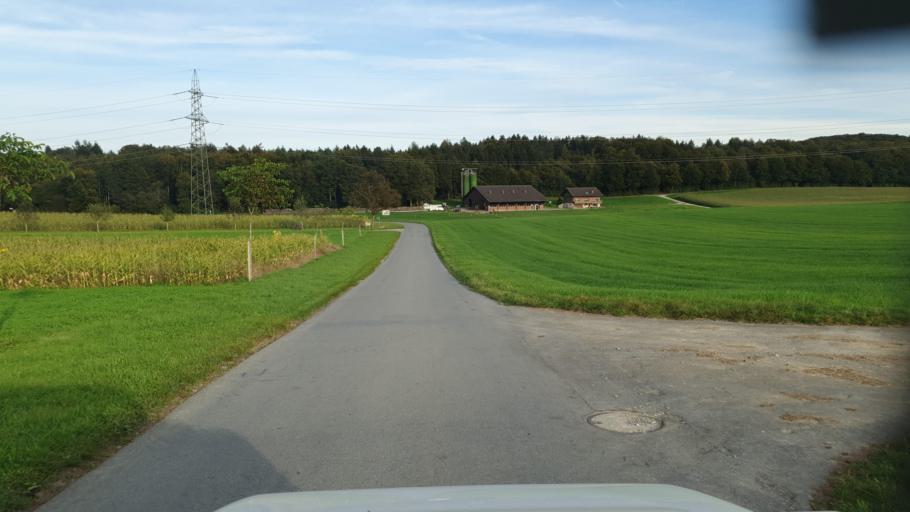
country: CH
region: Aargau
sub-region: Bezirk Muri
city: Auw
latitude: 47.2143
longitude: 8.3739
